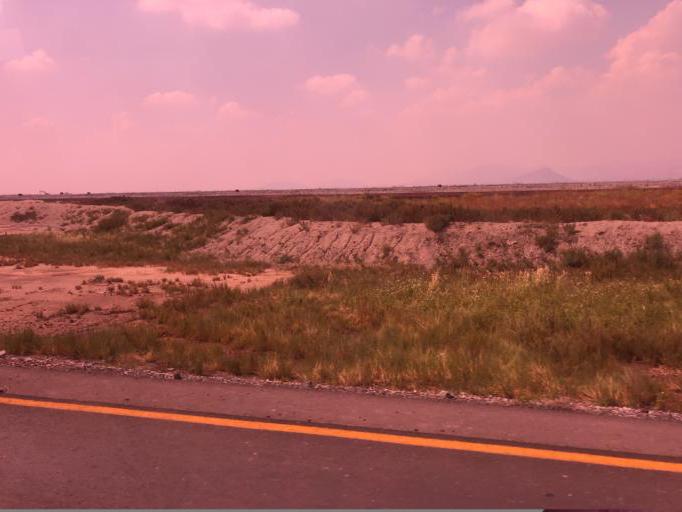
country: MX
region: Mexico
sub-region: Atenco
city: Colonia el Salado
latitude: 19.5399
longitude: -98.9851
